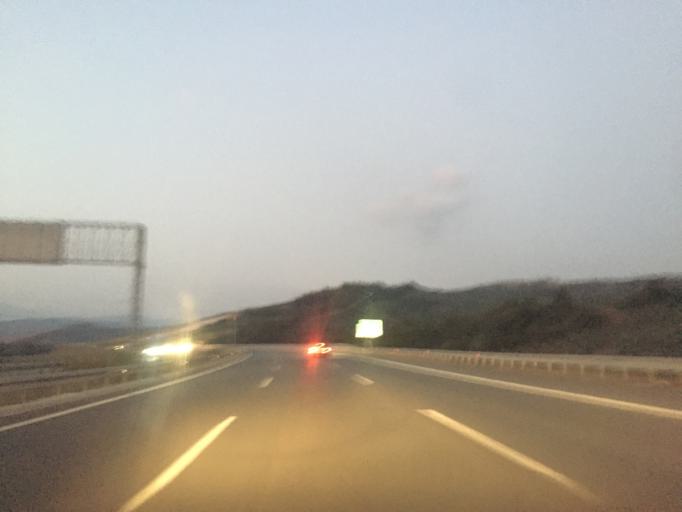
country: TR
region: Bursa
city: Demirtas
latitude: 40.3329
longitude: 29.1153
